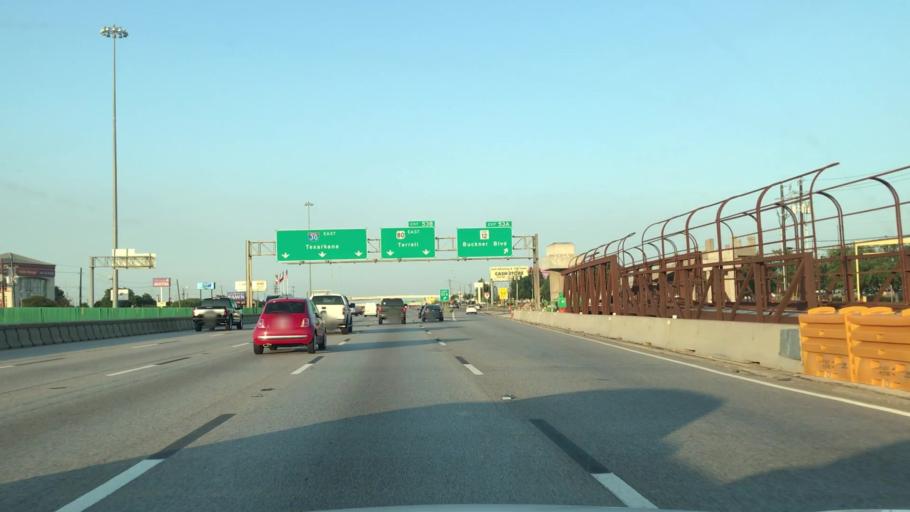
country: US
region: Texas
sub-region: Dallas County
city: Balch Springs
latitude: 32.7957
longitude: -96.6912
